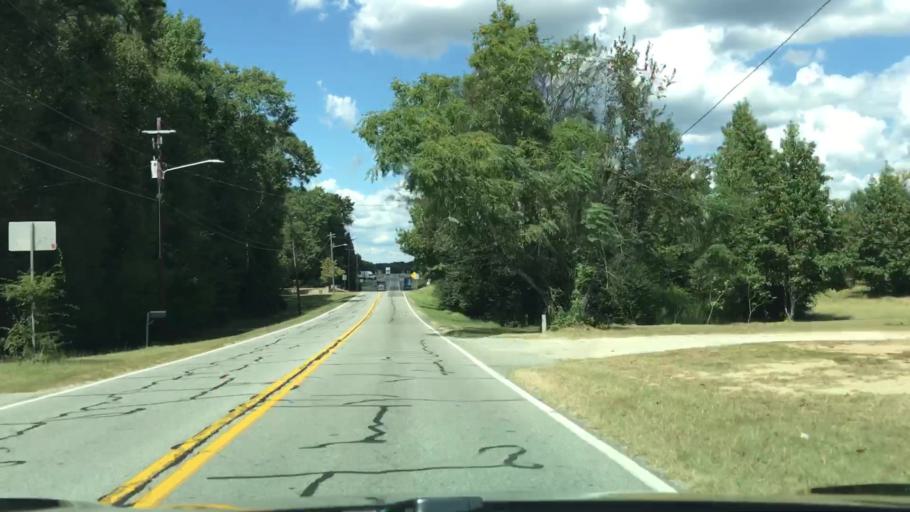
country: US
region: Georgia
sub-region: Greene County
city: Union Point
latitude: 33.5390
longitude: -83.0807
